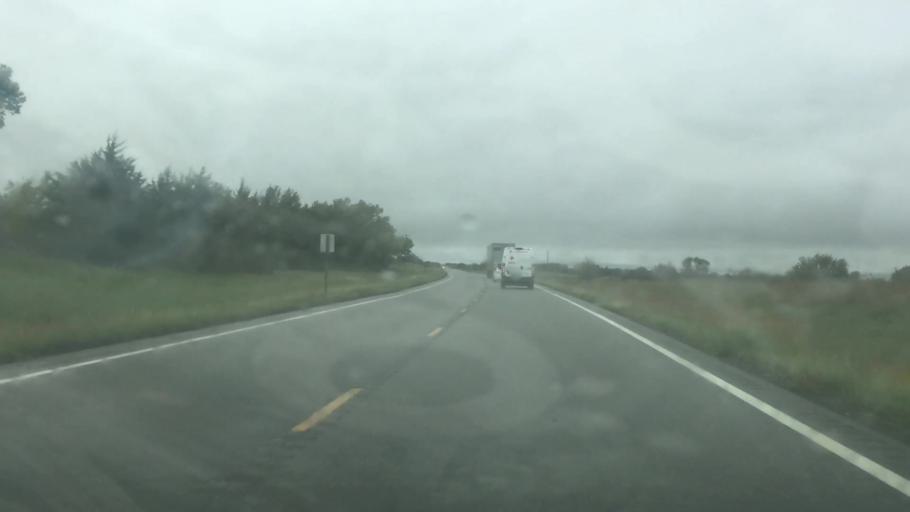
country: US
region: Kansas
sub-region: Anderson County
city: Garnett
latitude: 38.1427
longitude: -95.3281
